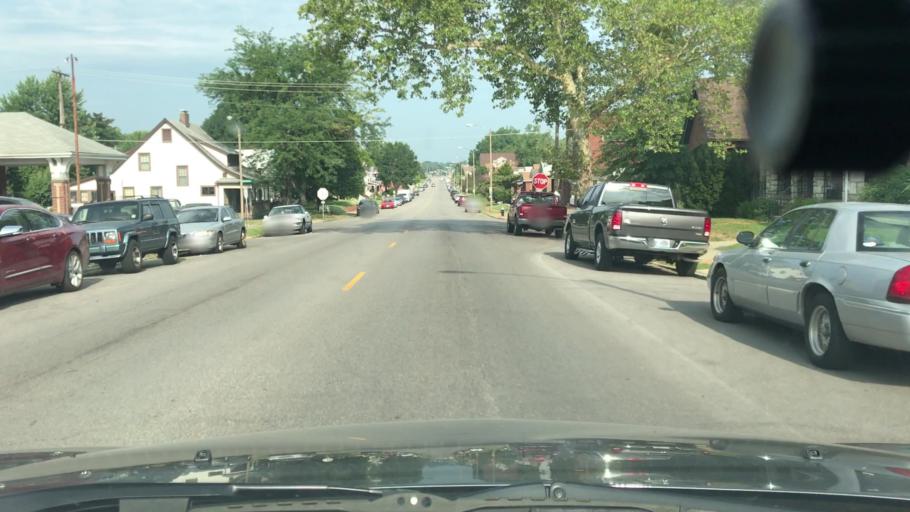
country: US
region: Missouri
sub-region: Saint Louis County
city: Maplewood
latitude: 38.6077
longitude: -90.2956
